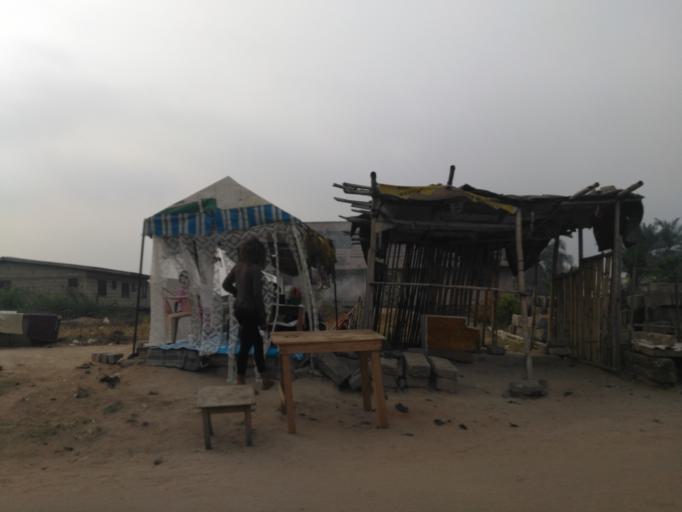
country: GH
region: Ashanti
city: Tafo
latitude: 6.7085
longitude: -1.6021
